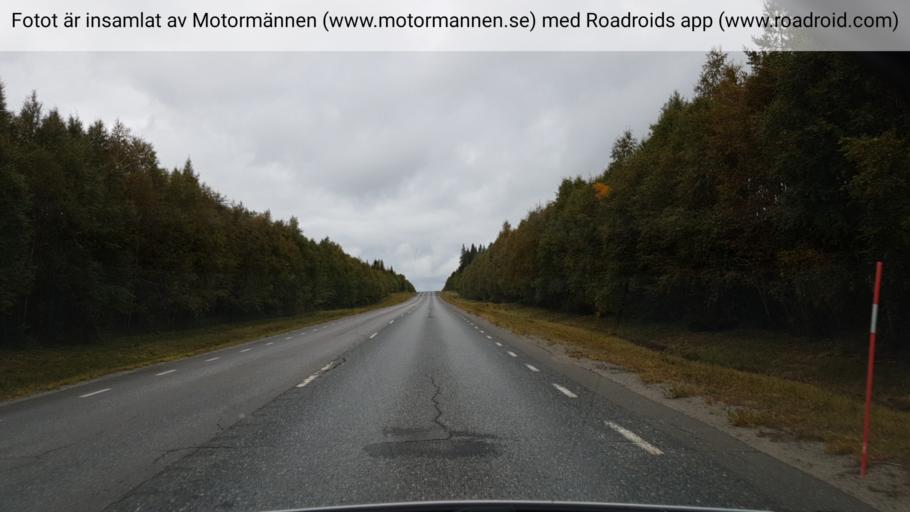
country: SE
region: Vaesterbotten
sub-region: Norsjo Kommun
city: Norsjoe
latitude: 64.9916
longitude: 19.3168
